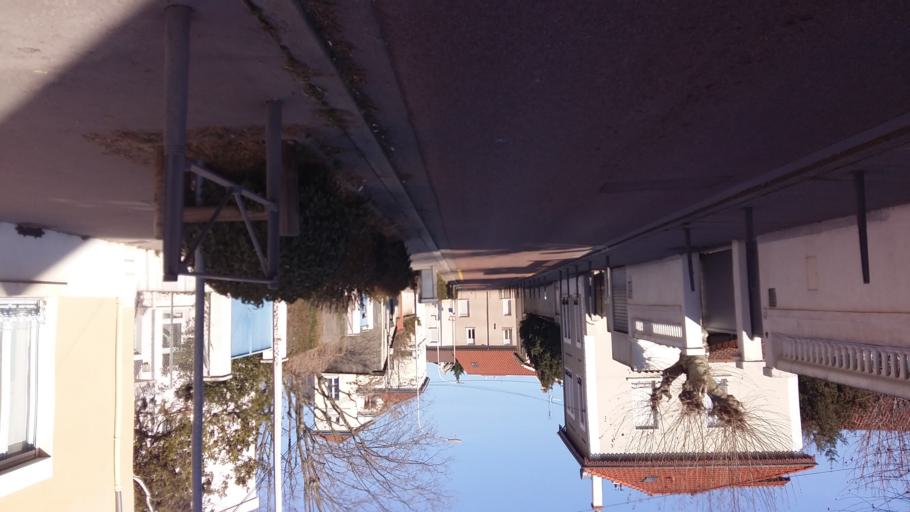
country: FR
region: Rhone-Alpes
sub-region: Departement du Rhone
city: Villeurbanne
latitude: 45.7475
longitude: 4.8856
